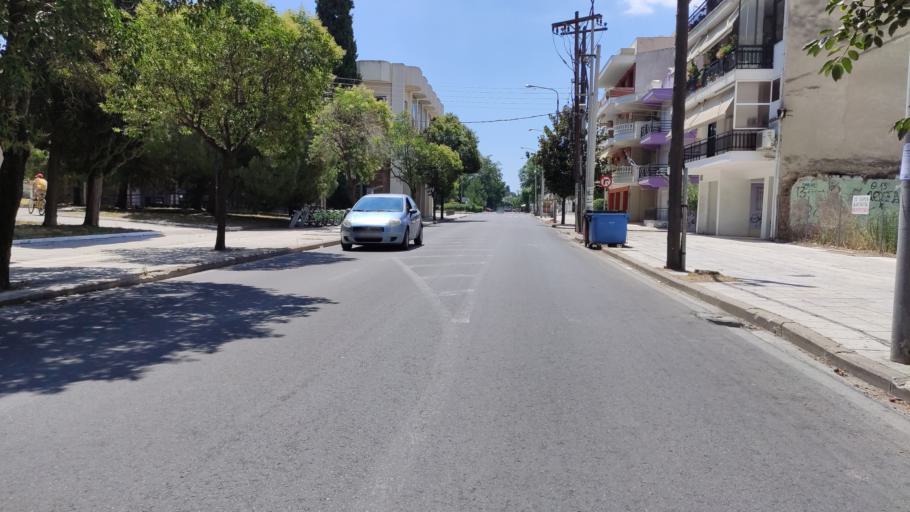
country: GR
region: East Macedonia and Thrace
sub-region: Nomos Rodopis
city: Komotini
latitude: 41.1158
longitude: 25.3982
